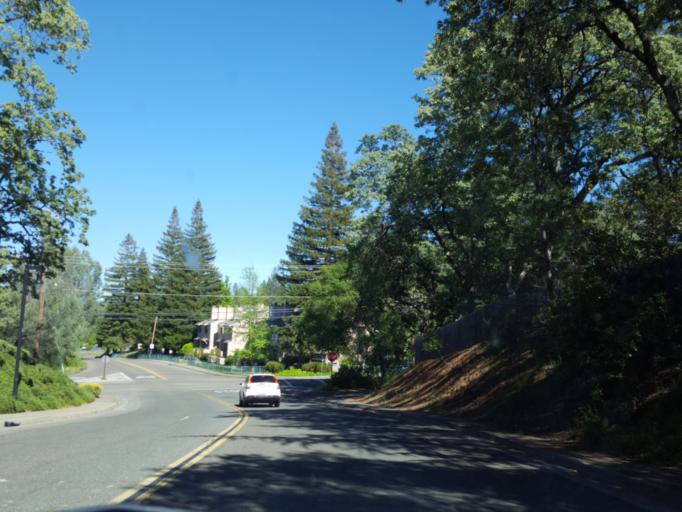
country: US
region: California
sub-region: Placer County
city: Auburn
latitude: 38.8855
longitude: -121.0768
